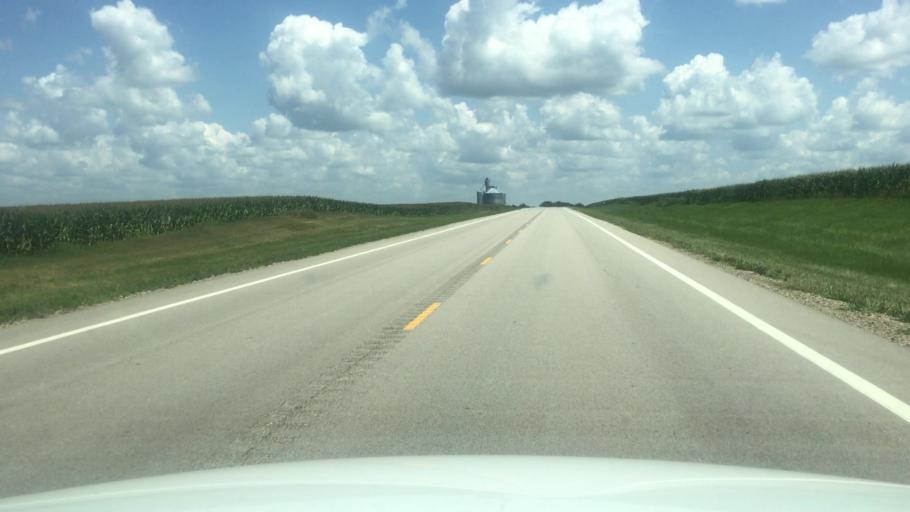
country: US
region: Kansas
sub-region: Brown County
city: Horton
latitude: 39.6601
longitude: -95.3948
